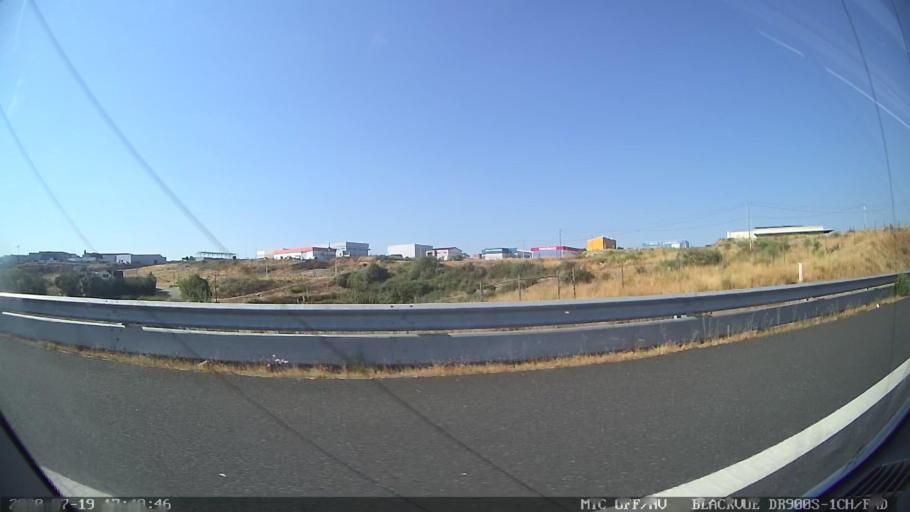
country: PT
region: Braganca
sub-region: Macedo de Cavaleiros
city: Macedo de Cavaleiros
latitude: 41.5693
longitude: -6.9848
